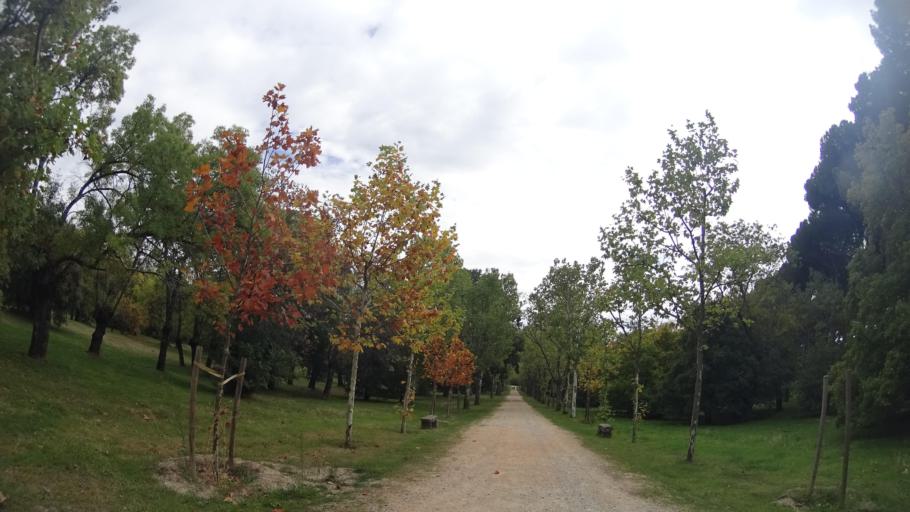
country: ES
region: Madrid
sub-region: Provincia de Madrid
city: San Lorenzo de El Escorial
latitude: 40.5873
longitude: -4.1400
